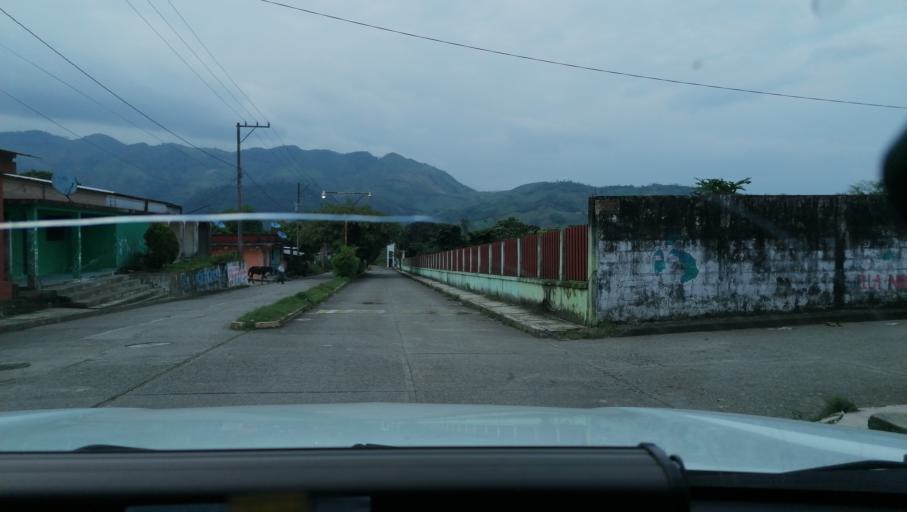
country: MX
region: Chiapas
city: Ixtacomitan
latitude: 17.3427
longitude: -93.1307
